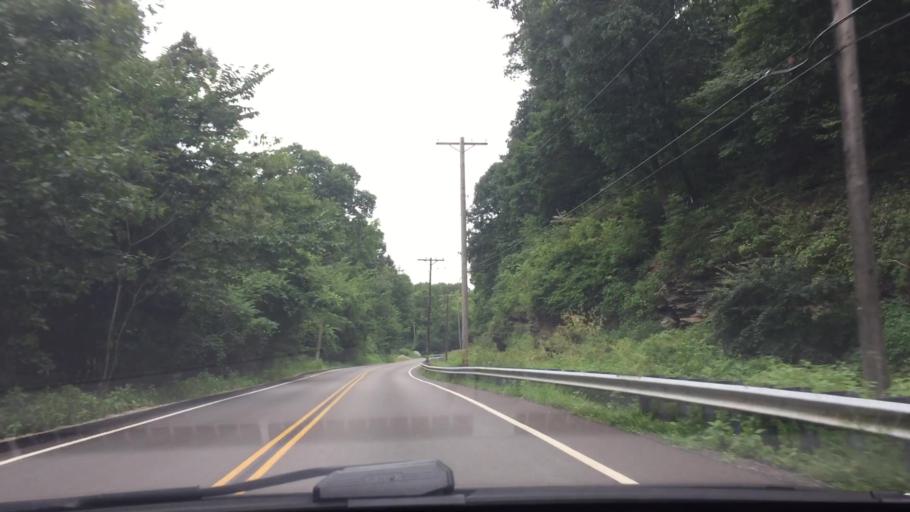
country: US
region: Pennsylvania
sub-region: Allegheny County
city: Rennerdale
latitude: 40.3881
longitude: -80.1574
